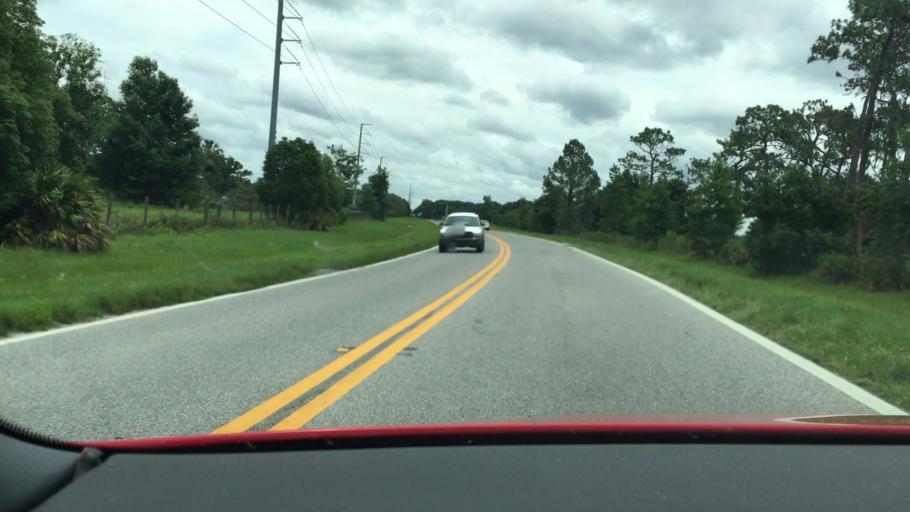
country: US
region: Florida
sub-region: Lake County
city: Eustis
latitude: 28.8694
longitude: -81.6595
